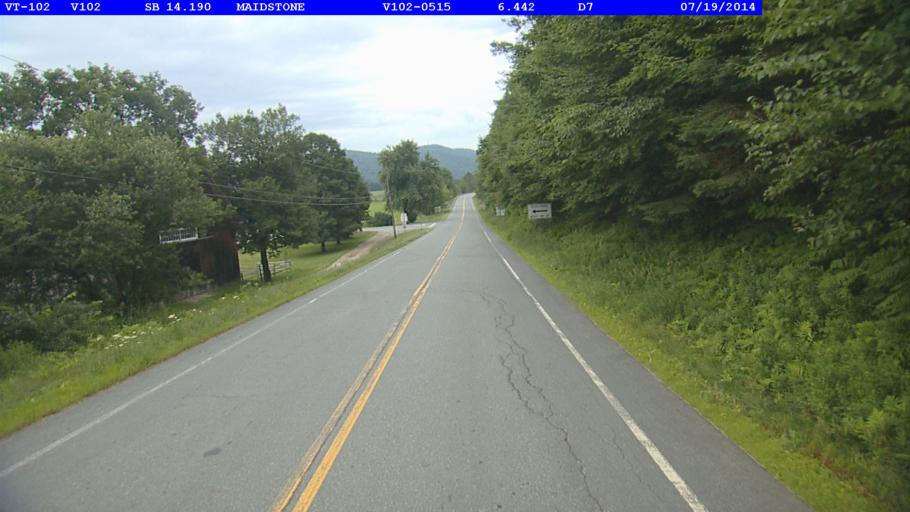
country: US
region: New Hampshire
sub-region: Coos County
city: Stratford
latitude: 44.6487
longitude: -71.5747
